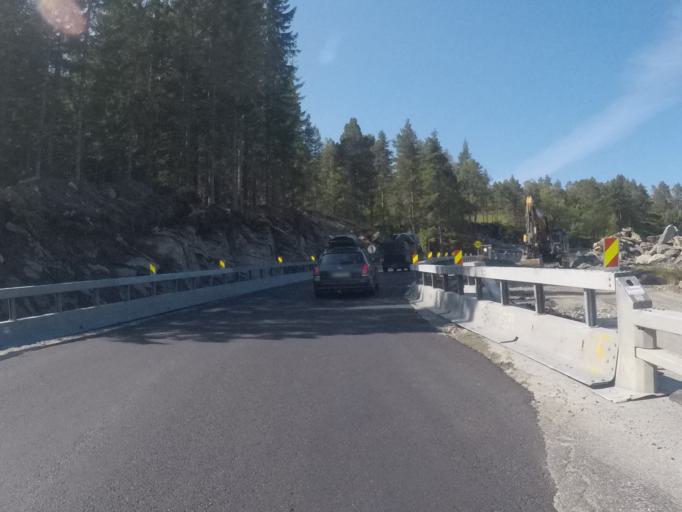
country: NO
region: Sogn og Fjordane
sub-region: Hornindal
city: Hornindal
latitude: 61.7924
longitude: 6.5098
